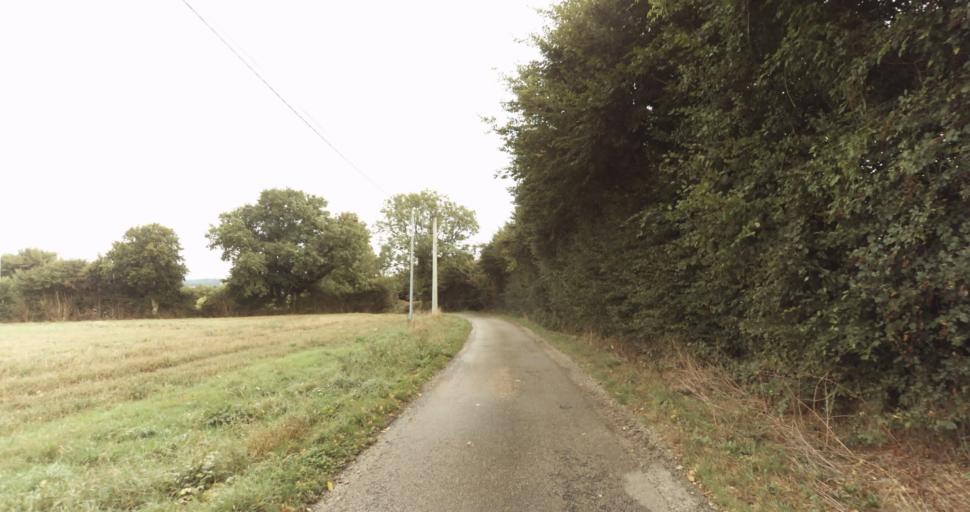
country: FR
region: Lower Normandy
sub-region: Departement de l'Orne
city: Vimoutiers
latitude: 48.8588
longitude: 0.1906
